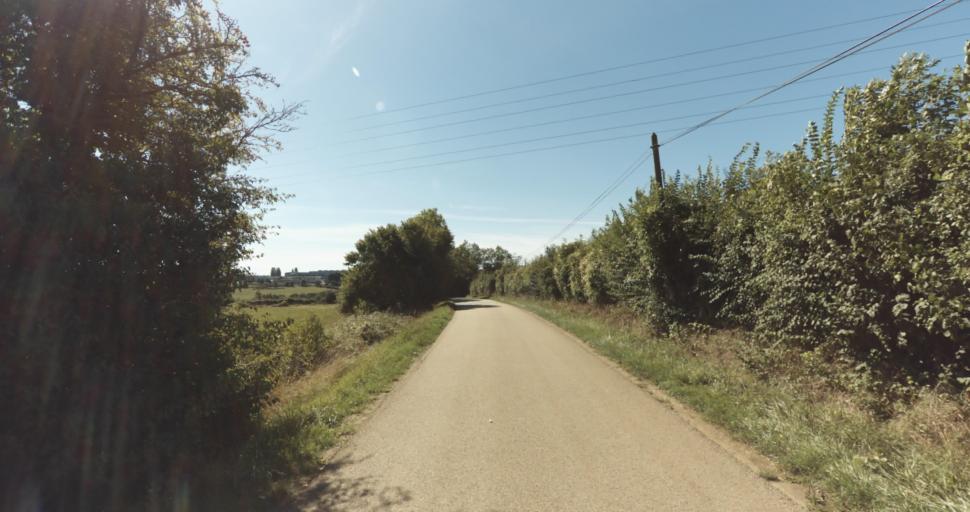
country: FR
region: Lower Normandy
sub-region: Departement de l'Orne
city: Gace
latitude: 48.7869
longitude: 0.2850
